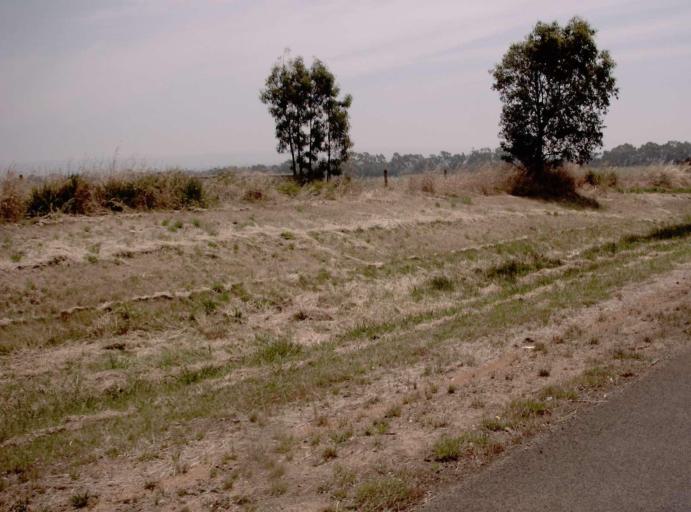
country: AU
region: Victoria
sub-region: Latrobe
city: Traralgon
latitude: -38.2452
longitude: 146.6244
